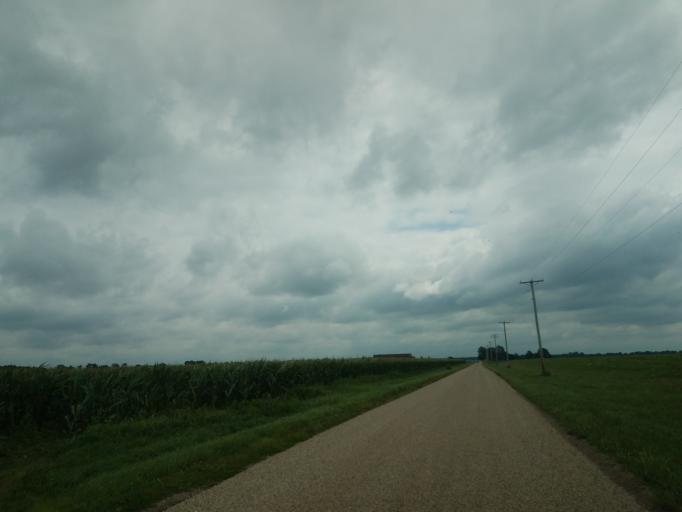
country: US
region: Illinois
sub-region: McLean County
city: Twin Grove
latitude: 40.4369
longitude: -89.0622
